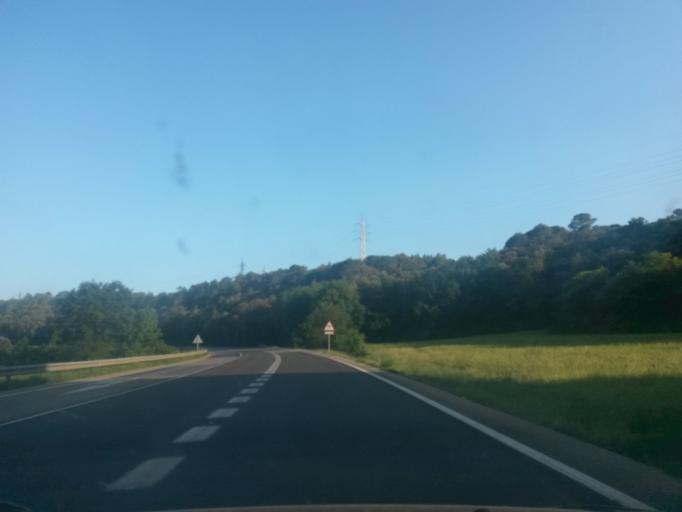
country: ES
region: Catalonia
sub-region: Provincia de Girona
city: Besalu
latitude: 42.1845
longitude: 2.7365
